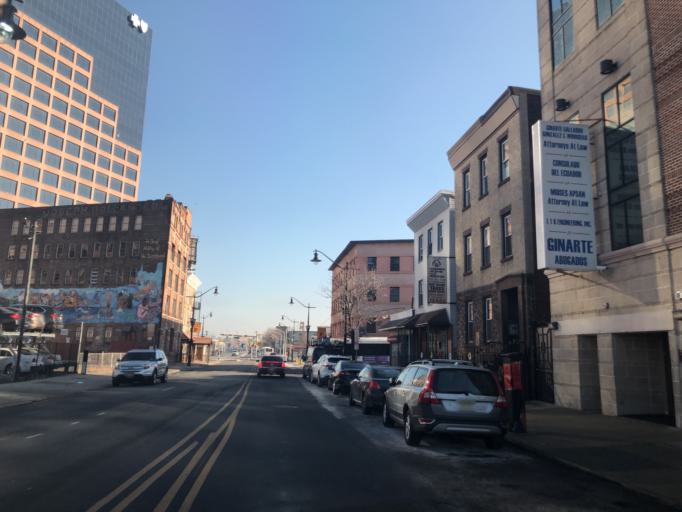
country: US
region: New Jersey
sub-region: Essex County
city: Newark
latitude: 40.7335
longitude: -74.1629
